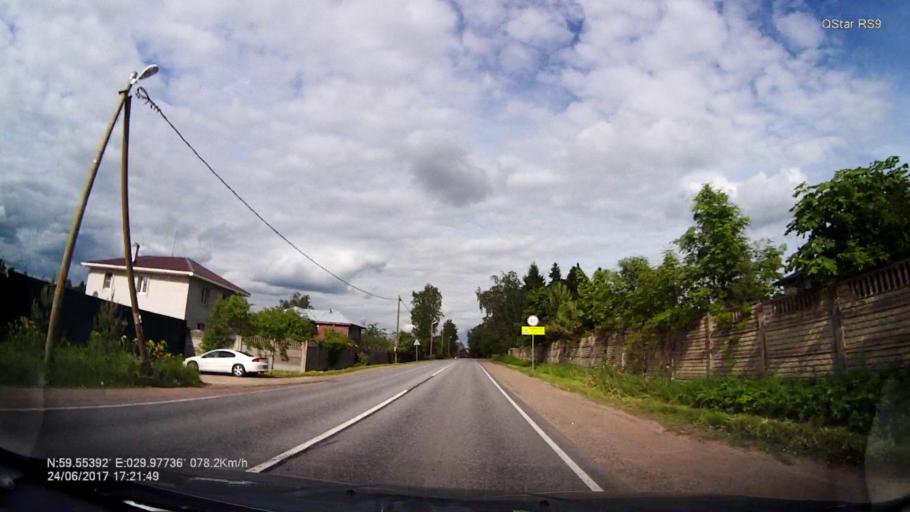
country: RU
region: Leningrad
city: Voyskovitsy
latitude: 59.5541
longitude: 29.9780
